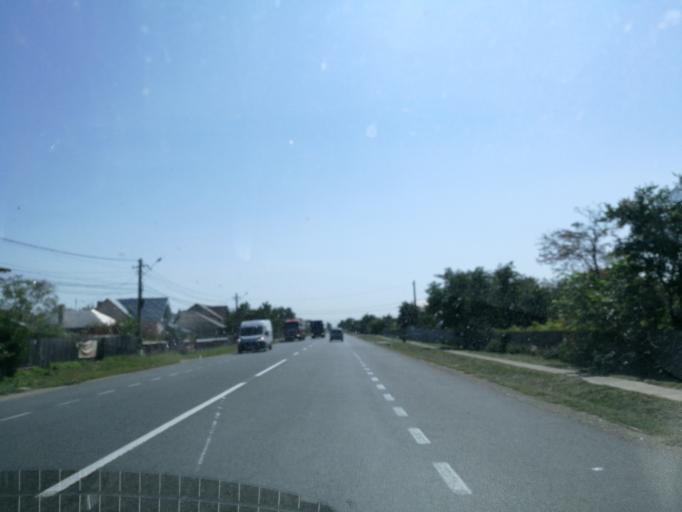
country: RO
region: Bacau
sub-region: Comuna Parava
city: Parava
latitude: 46.3252
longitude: 27.0127
